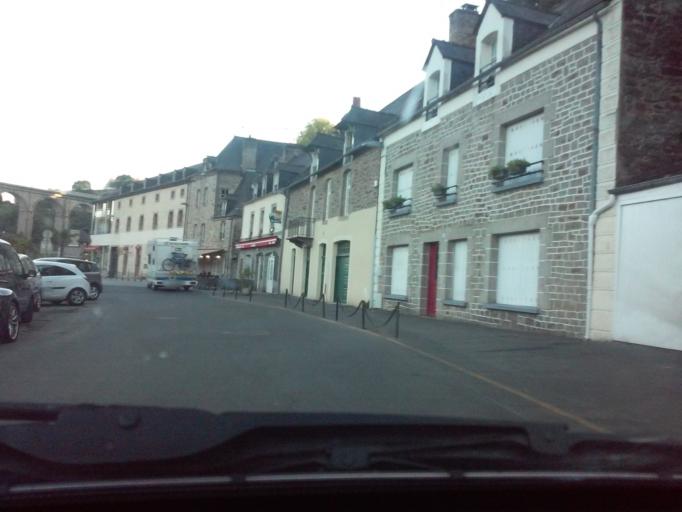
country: FR
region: Brittany
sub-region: Departement des Cotes-d'Armor
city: Dinan
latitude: 48.4579
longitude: -2.0377
